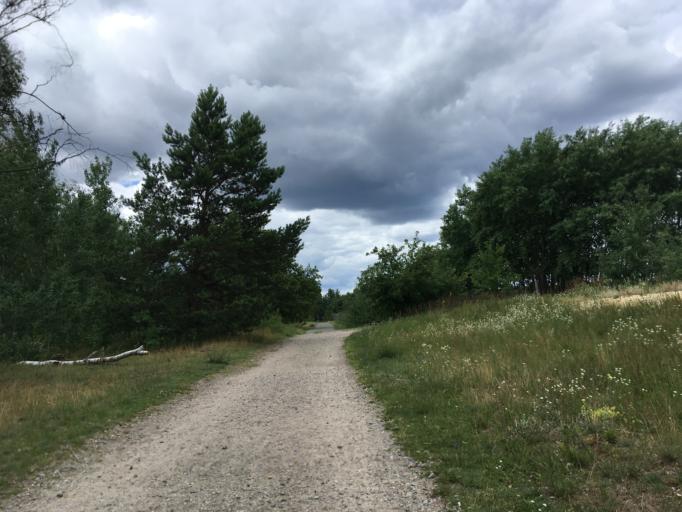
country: DE
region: Berlin
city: Buch
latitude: 52.6823
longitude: 13.5168
